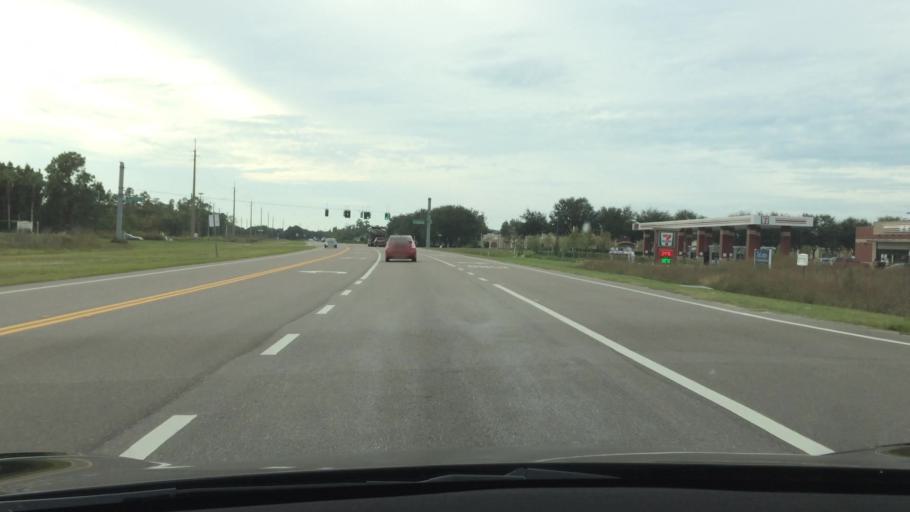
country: US
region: Florida
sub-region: Hillsborough County
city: Keystone
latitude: 28.1855
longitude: -82.6343
